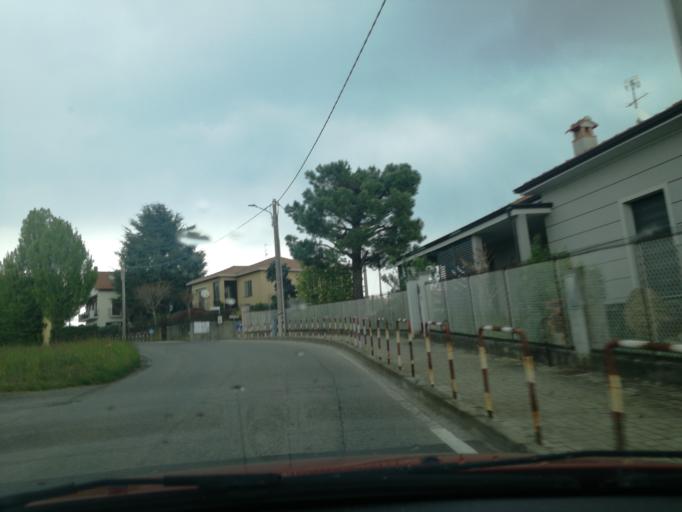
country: IT
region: Lombardy
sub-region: Provincia di Monza e Brianza
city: Correzzana
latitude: 45.6739
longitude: 9.3034
